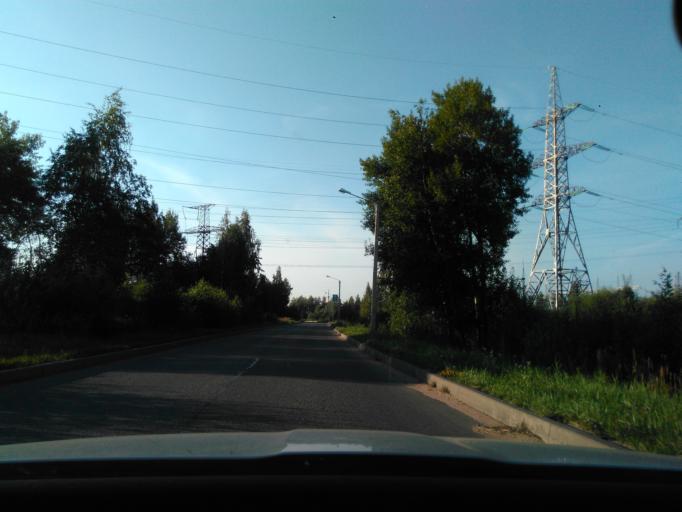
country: RU
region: Tverskaya
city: Konakovo
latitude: 56.7402
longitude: 36.7796
